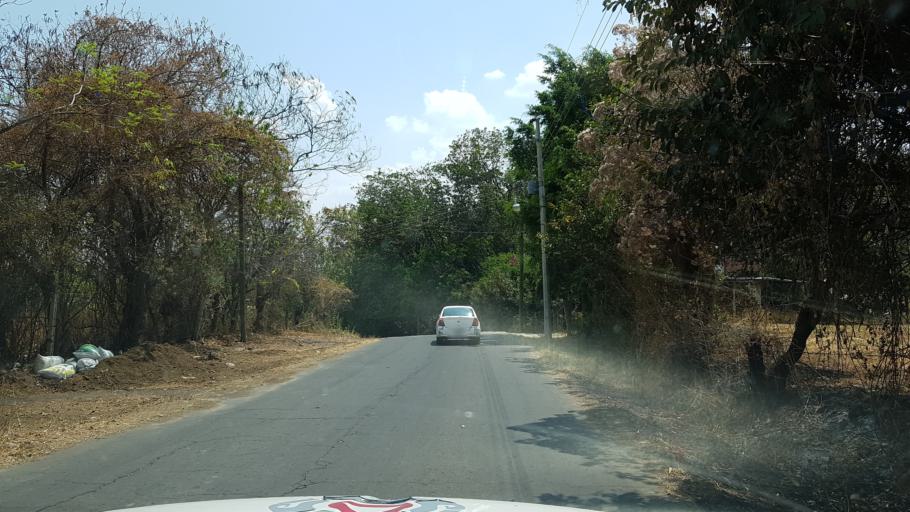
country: MX
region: Morelos
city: Ocuituco
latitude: 18.8913
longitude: -98.8106
